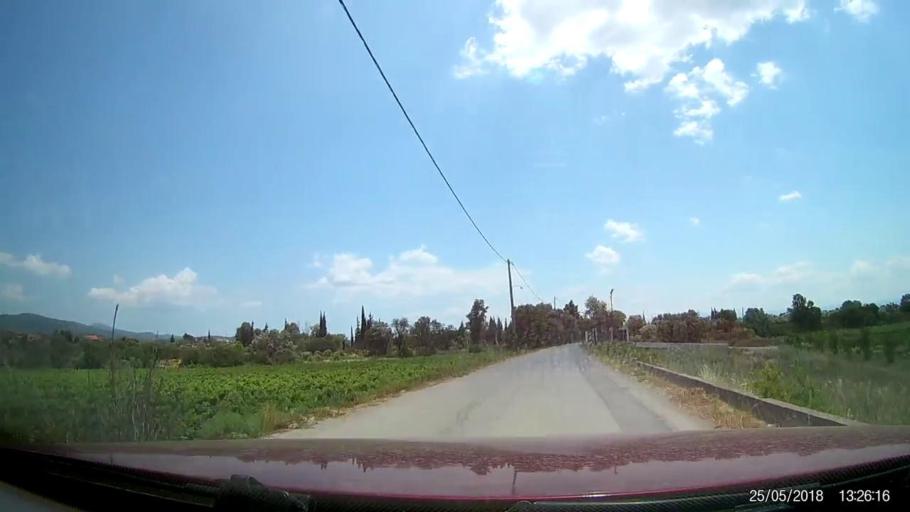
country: GR
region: Central Greece
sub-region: Nomos Evvoias
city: Mytikas
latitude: 38.4571
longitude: 23.6473
